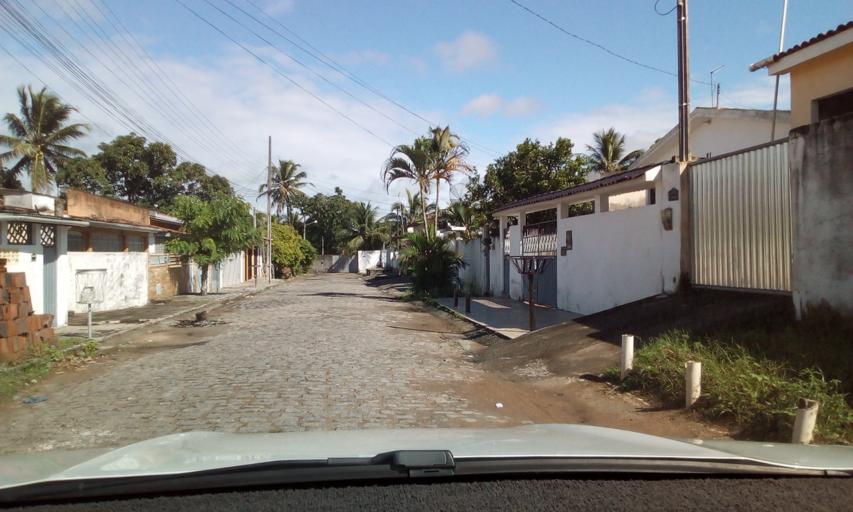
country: BR
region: Paraiba
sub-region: Santa Rita
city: Santa Rita
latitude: -7.1246
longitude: -34.9749
